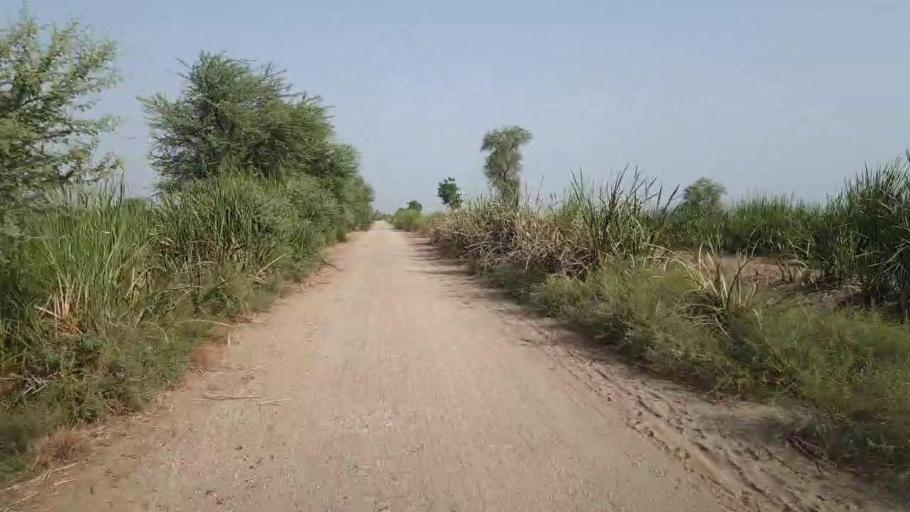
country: PK
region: Sindh
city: Daur
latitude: 26.3350
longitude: 68.1868
